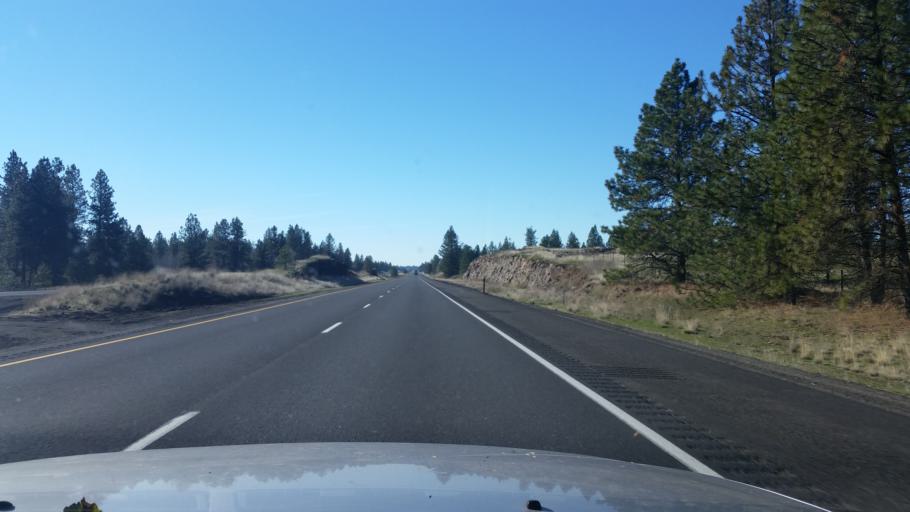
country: US
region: Washington
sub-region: Spokane County
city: Medical Lake
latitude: 47.4639
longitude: -117.7506
